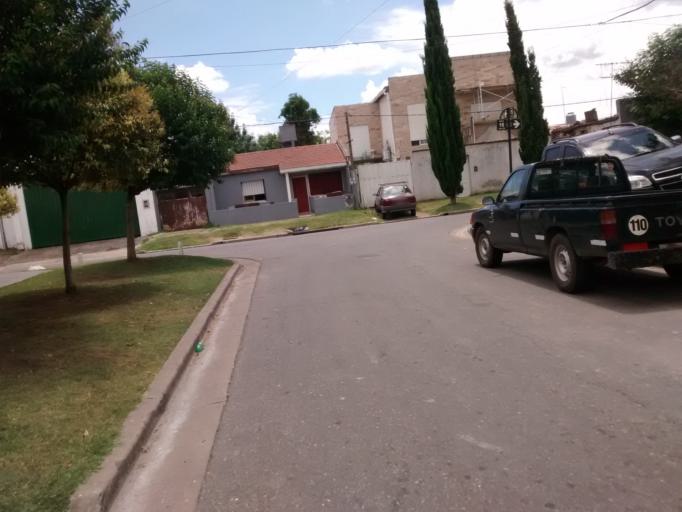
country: AR
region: Buenos Aires
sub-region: Partido de La Plata
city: La Plata
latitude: -34.9419
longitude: -57.9341
